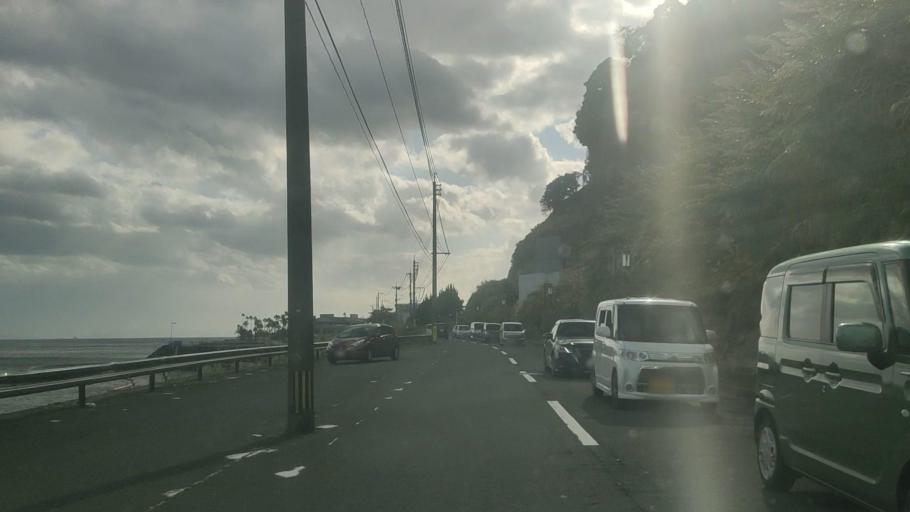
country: JP
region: Kagoshima
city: Kagoshima-shi
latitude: 31.6115
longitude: 130.5751
